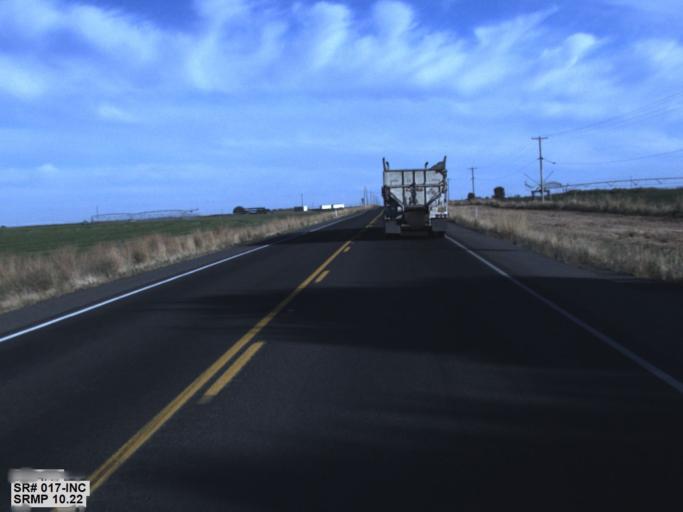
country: US
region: Washington
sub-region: Franklin County
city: Basin City
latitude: 46.6004
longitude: -119.0063
